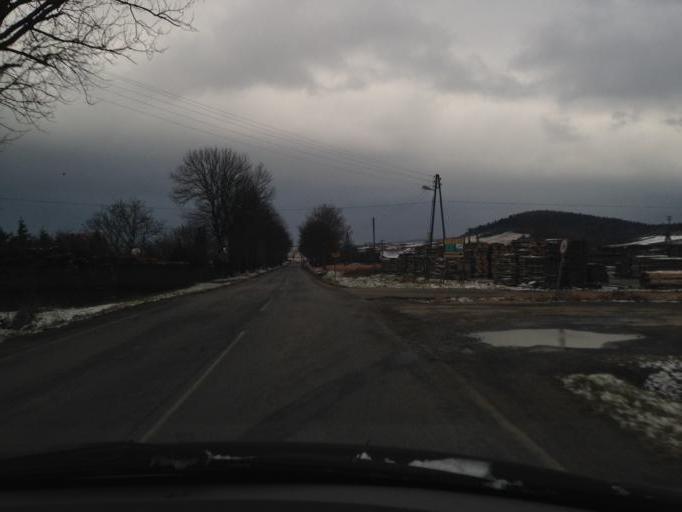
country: PL
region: Subcarpathian Voivodeship
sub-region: Powiat jasielski
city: Osiek Jasielski
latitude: 49.6119
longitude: 21.4735
